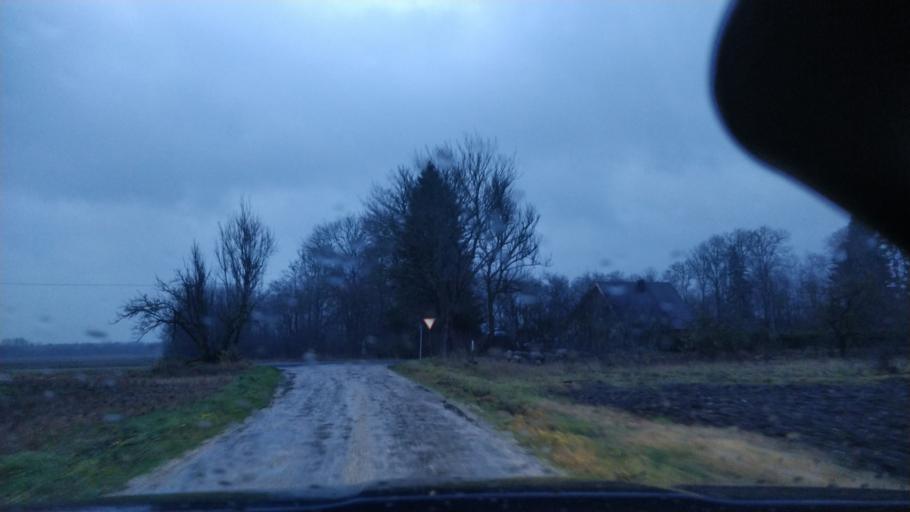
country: EE
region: Laeaene
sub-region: Lihula vald
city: Lihula
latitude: 58.8552
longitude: 24.0093
